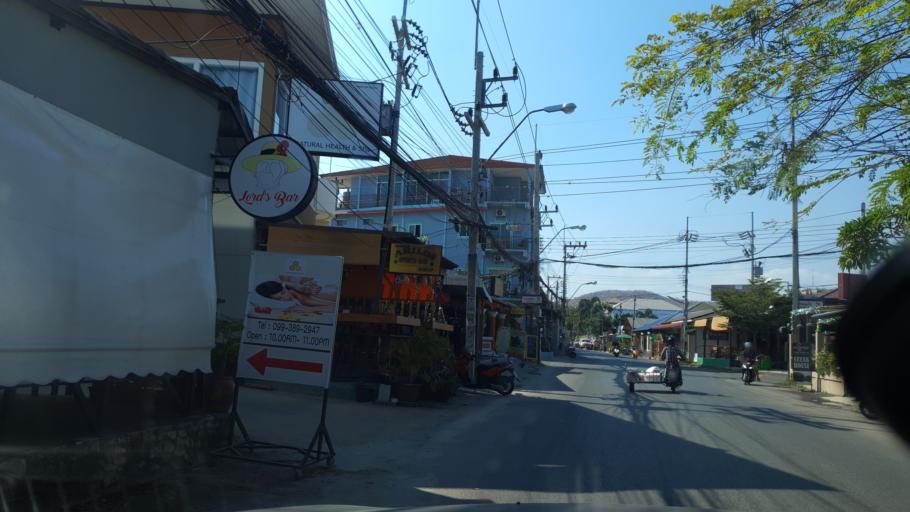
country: TH
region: Prachuap Khiri Khan
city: Hua Hin
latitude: 12.5545
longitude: 99.9549
